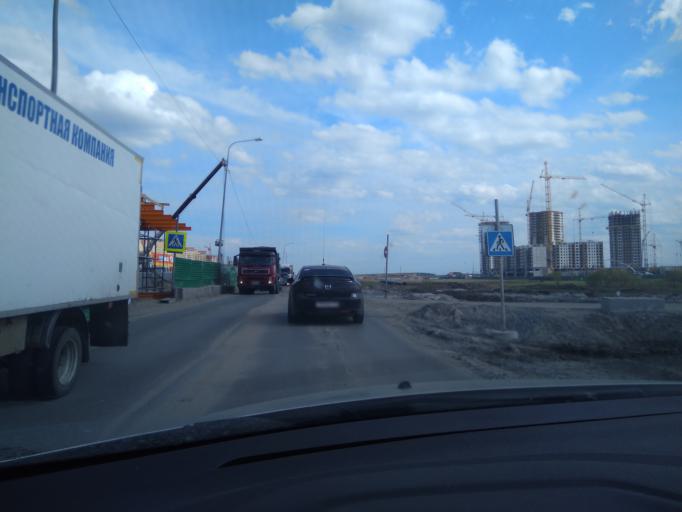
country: RU
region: Tjumen
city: Tyumen
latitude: 57.1036
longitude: 65.5649
